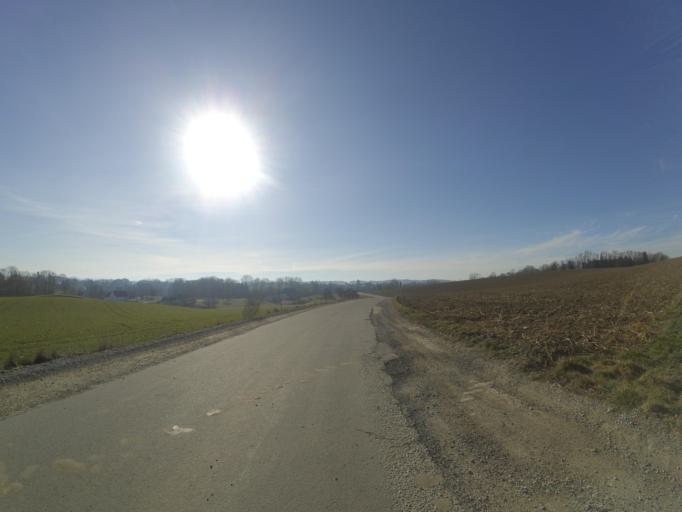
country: DE
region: Baden-Wuerttemberg
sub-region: Tuebingen Region
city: Aulendorf
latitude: 47.9366
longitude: 9.6383
